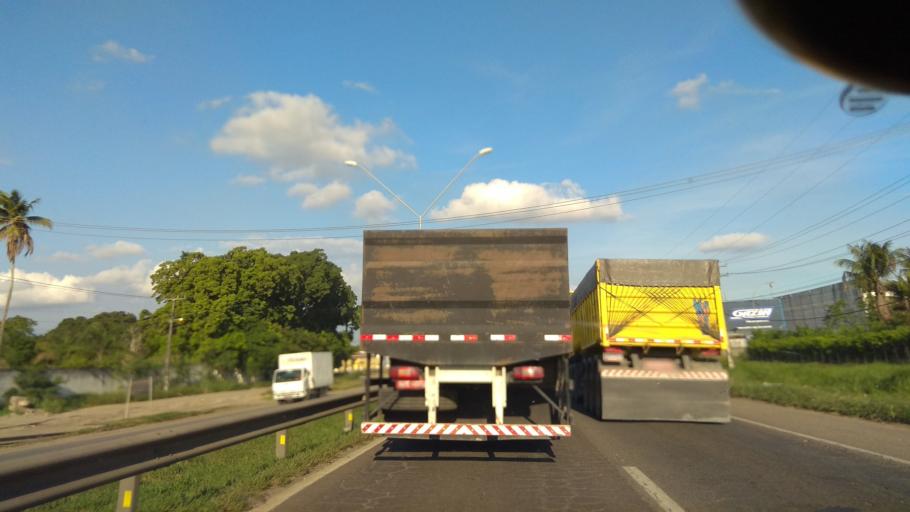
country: BR
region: Bahia
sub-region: Feira De Santana
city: Feira de Santana
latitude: -12.3064
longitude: -38.8905
